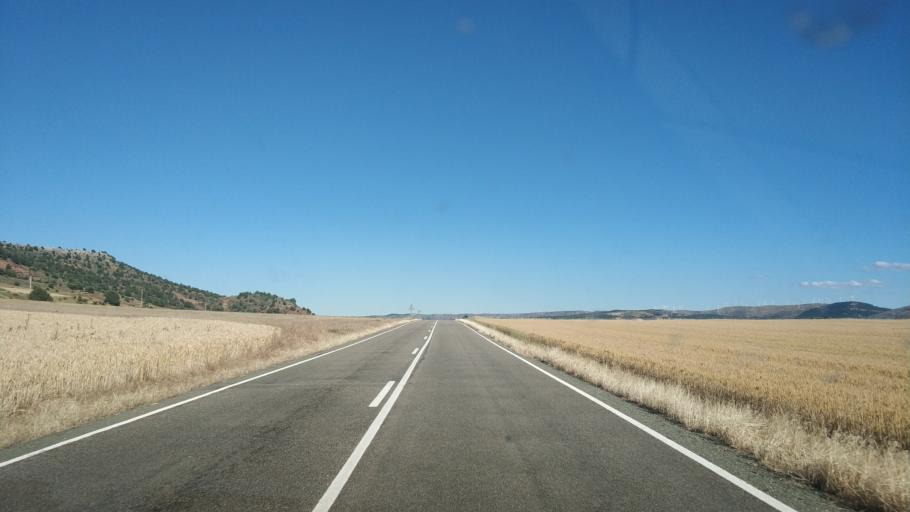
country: ES
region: Castille and Leon
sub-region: Provincia de Soria
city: Montejo de Tiermes
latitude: 41.3536
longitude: -3.1698
